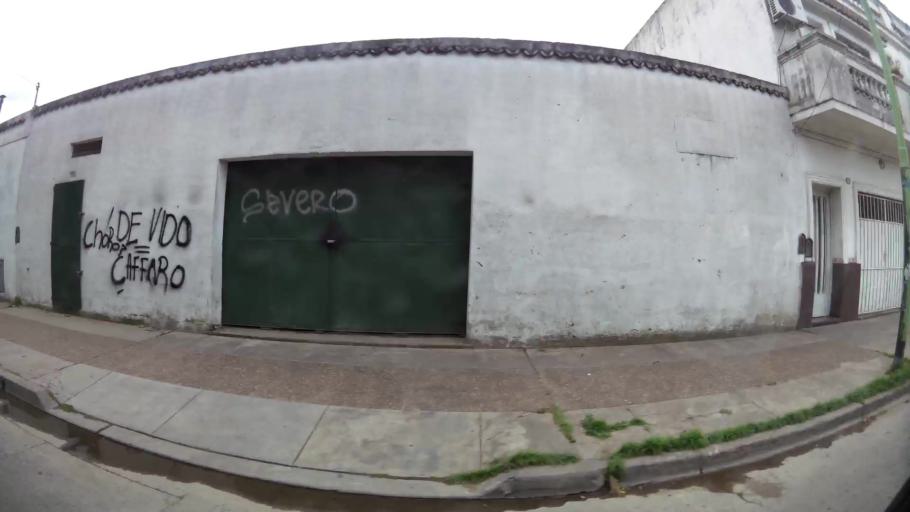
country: AR
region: Buenos Aires
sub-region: Partido de Zarate
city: Zarate
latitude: -34.1069
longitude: -59.0198
